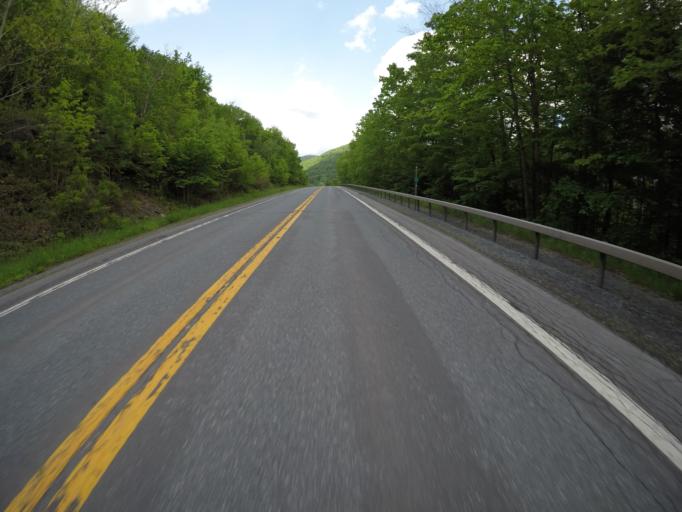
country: US
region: New York
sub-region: Delaware County
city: Stamford
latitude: 42.1531
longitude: -74.6277
